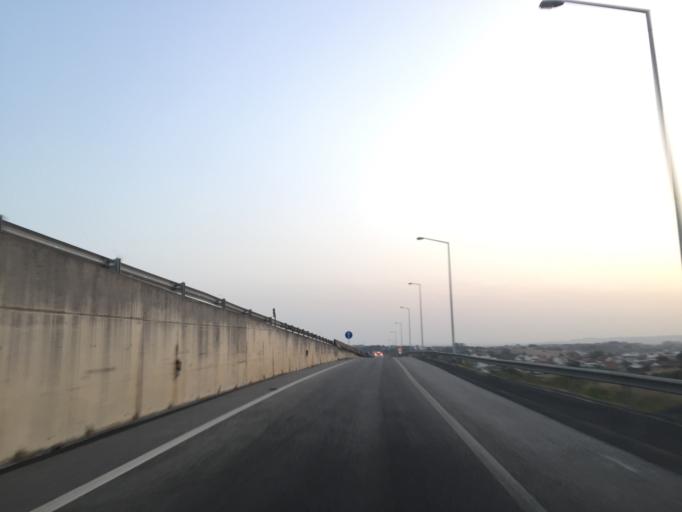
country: PT
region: Lisbon
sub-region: Azambuja
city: Aveiras de Cima
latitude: 39.1401
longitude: -8.8898
